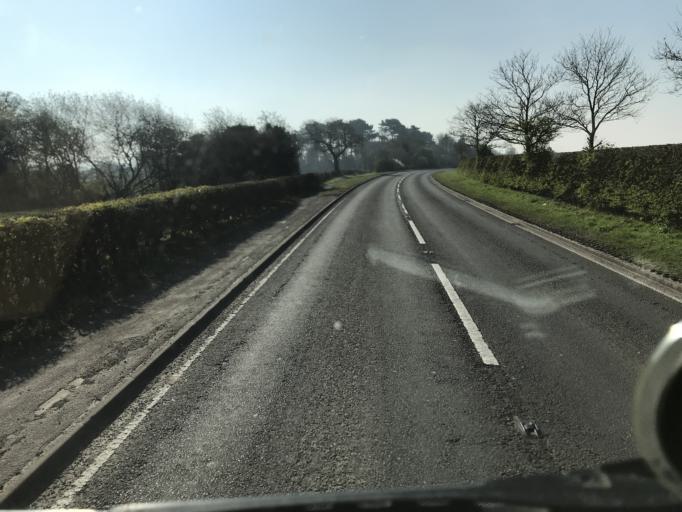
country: GB
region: England
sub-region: Cheshire West and Chester
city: Waverton
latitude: 53.1584
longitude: -2.8132
